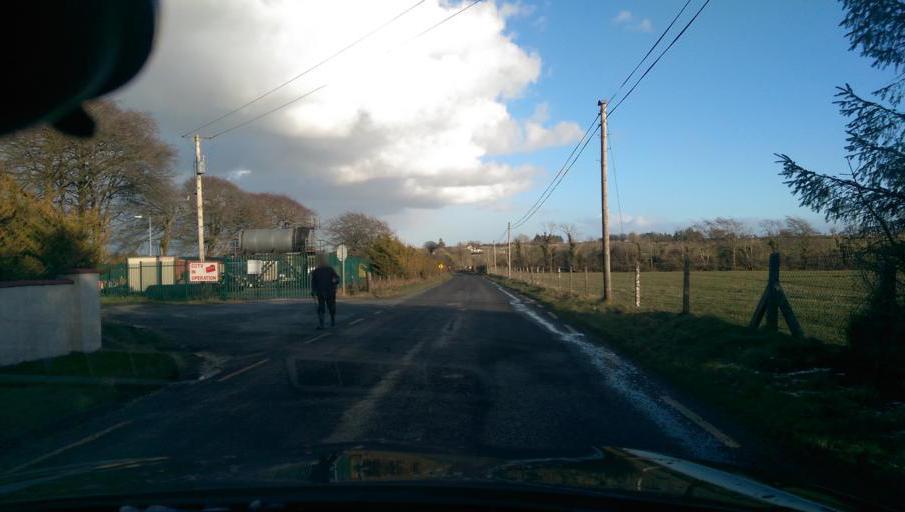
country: IE
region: Connaught
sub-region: County Galway
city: Loughrea
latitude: 53.4184
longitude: -8.5187
